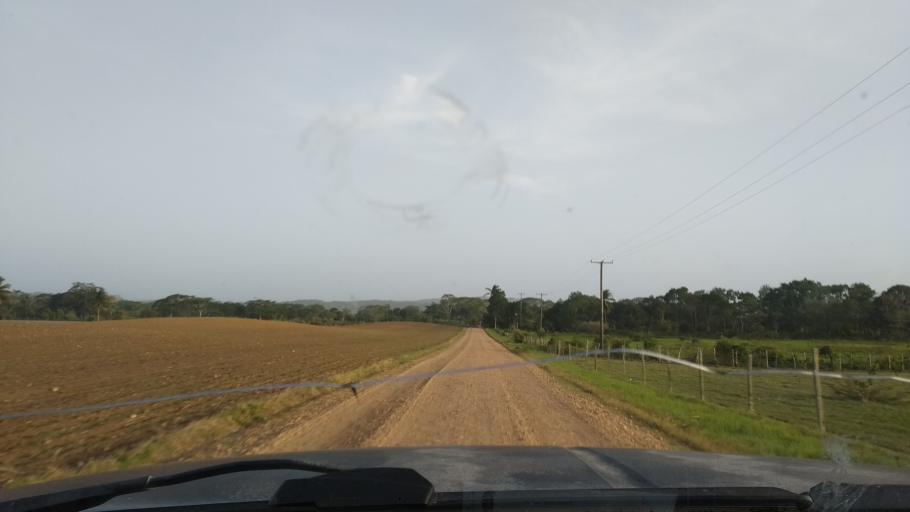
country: BZ
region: Cayo
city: San Ignacio
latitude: 17.2106
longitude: -89.0137
